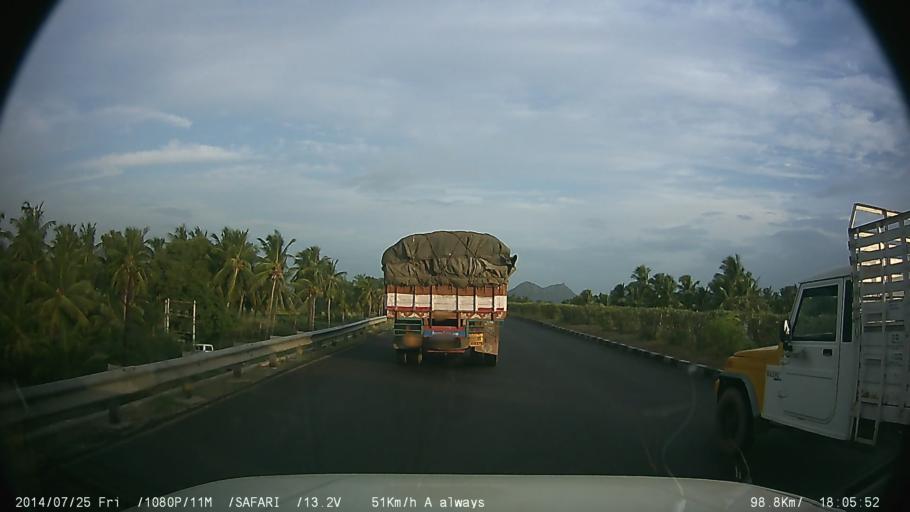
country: IN
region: Tamil Nadu
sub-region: Krishnagiri
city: Kaverippattanam
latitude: 12.4334
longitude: 78.2236
